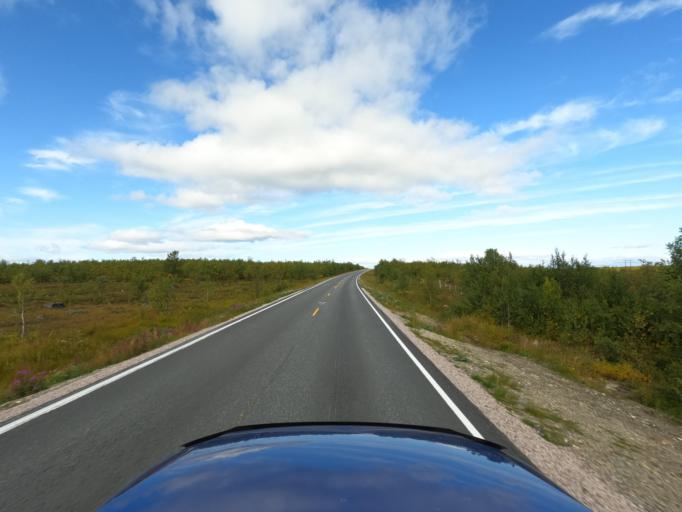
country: NO
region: Finnmark Fylke
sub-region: Karasjok
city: Karasjohka
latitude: 69.6440
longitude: 25.2822
